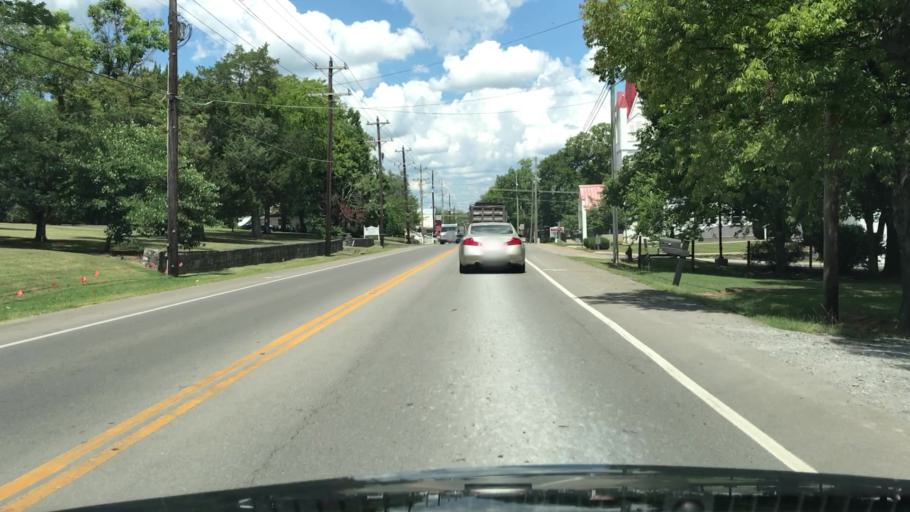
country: US
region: Tennessee
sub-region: Williamson County
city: Nolensville
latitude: 35.9510
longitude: -86.6686
